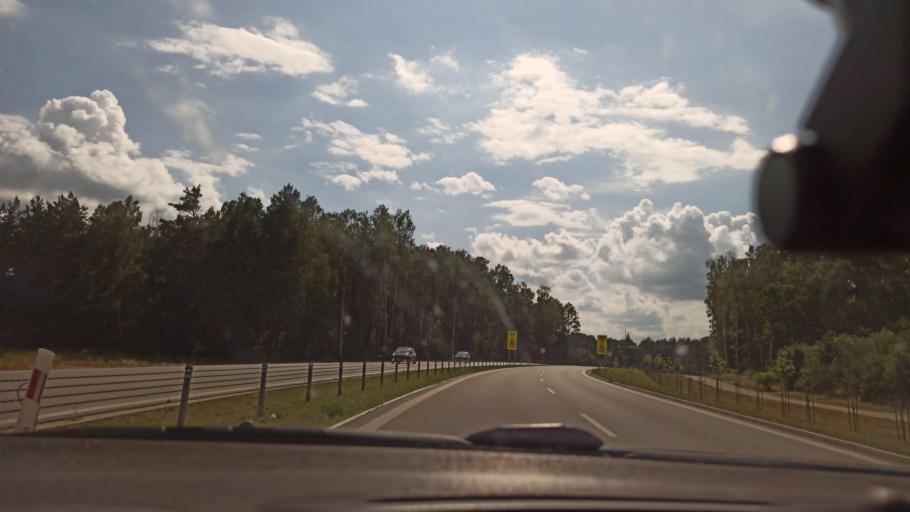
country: PL
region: Podlasie
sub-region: Powiat bialostocki
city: Turosn Koscielna
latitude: 53.0601
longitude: 23.0621
